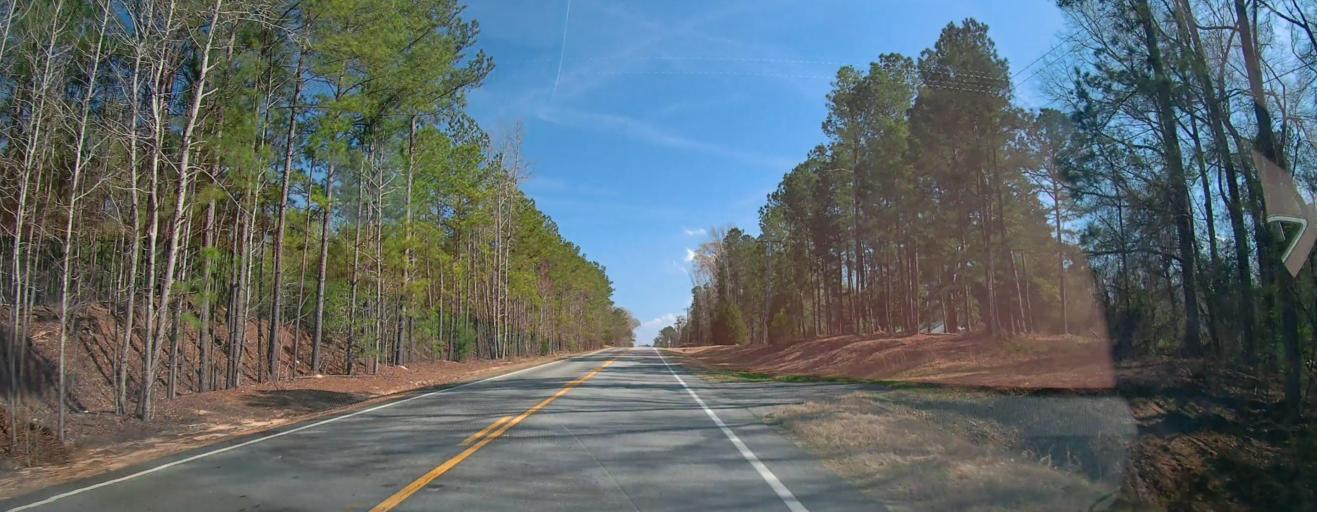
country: US
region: Georgia
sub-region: Wilkinson County
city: Gordon
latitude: 32.8988
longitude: -83.3673
